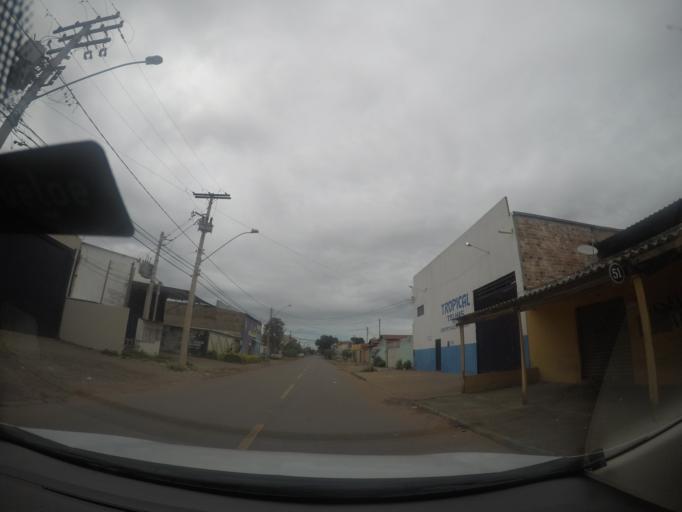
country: BR
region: Goias
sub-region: Goiania
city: Goiania
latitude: -16.7007
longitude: -49.3231
